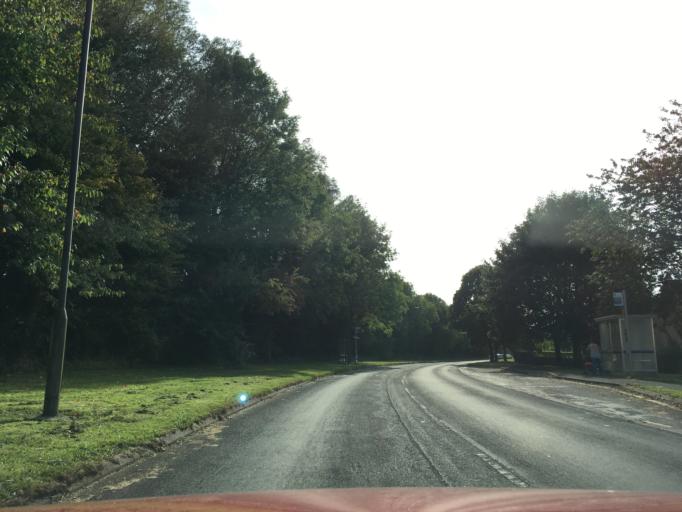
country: GB
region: England
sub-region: South Gloucestershire
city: Yate
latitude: 51.5260
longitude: -2.4152
